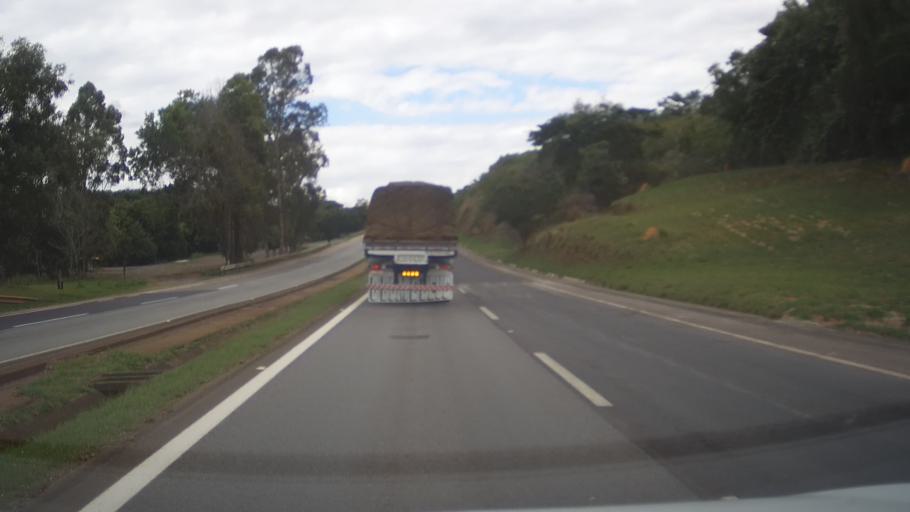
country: BR
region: Minas Gerais
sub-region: Itauna
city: Itauna
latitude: -20.3199
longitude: -44.4553
